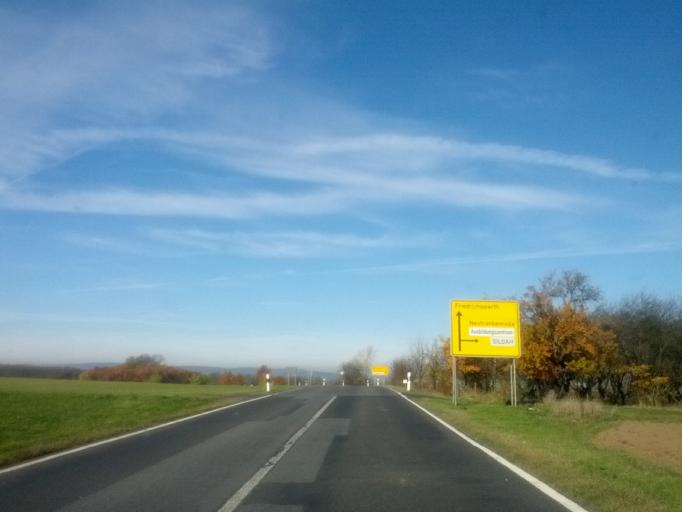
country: DE
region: Thuringia
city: Friedrichswerth
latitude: 50.9633
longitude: 10.5537
